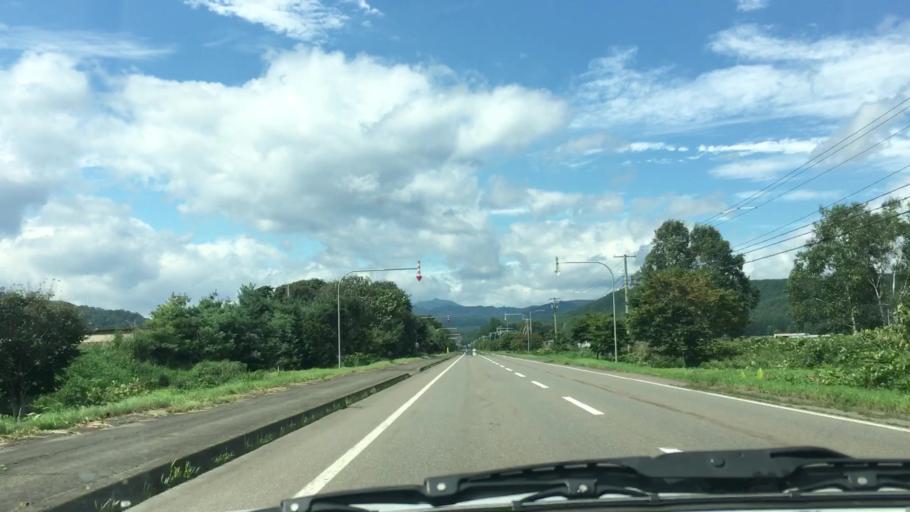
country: JP
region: Hokkaido
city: Otofuke
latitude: 43.3122
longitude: 143.3073
